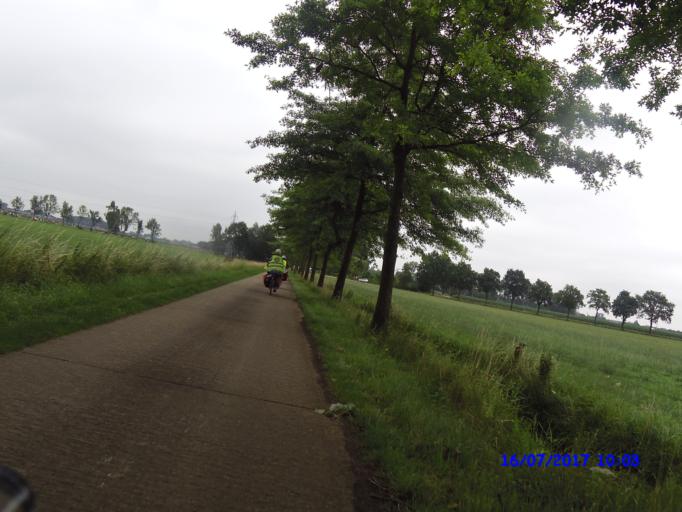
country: BE
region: Flanders
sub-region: Provincie Antwerpen
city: Lille
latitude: 51.2294
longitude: 4.8734
